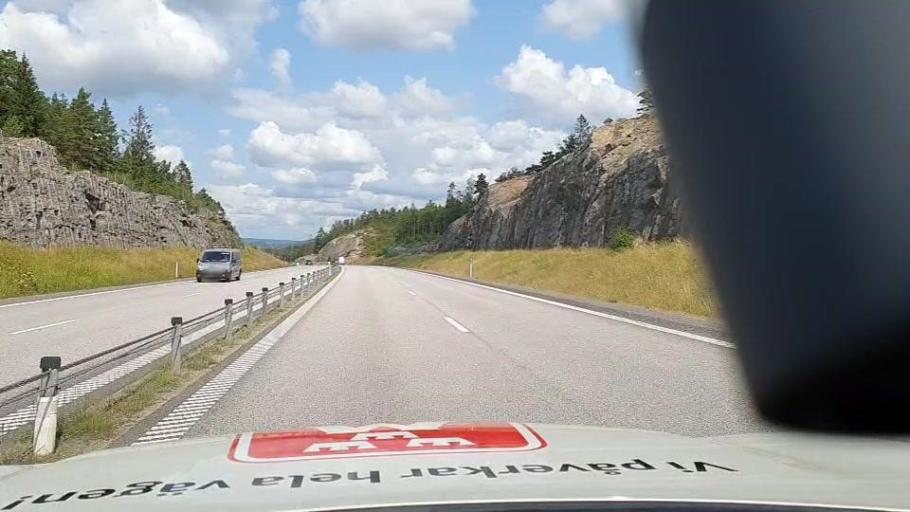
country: SE
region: Vaestra Goetaland
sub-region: Lilla Edets Kommun
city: Lodose
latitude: 58.0562
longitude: 12.1679
